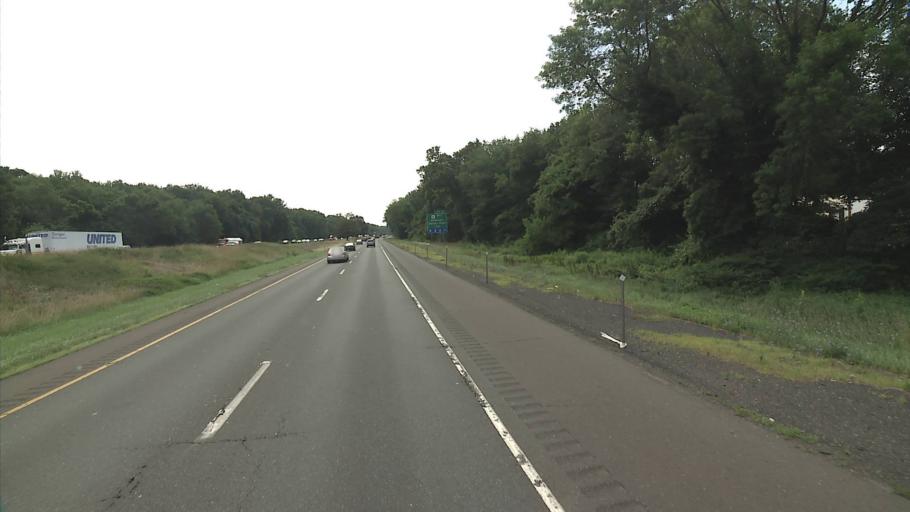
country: US
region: Connecticut
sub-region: Fairfield County
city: Newtown
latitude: 41.4266
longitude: -73.3077
